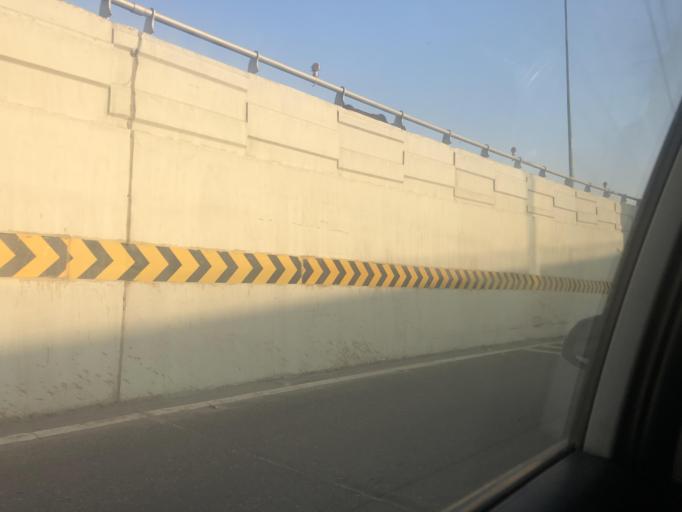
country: IN
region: Haryana
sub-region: Gurgaon
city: Gurgaon
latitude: 28.4860
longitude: 77.0952
